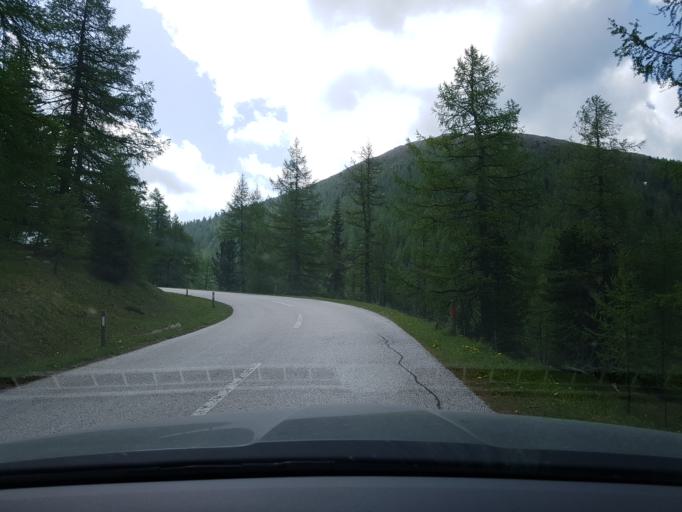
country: AT
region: Salzburg
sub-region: Politischer Bezirk Tamsweg
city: Thomatal
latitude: 46.9408
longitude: 13.7350
